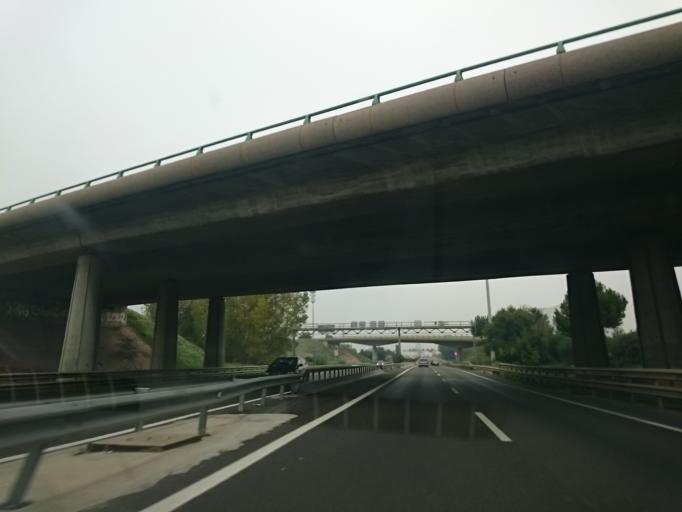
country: ES
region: Catalonia
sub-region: Provincia de Barcelona
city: El Prat de Llobregat
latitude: 41.3212
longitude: 2.0743
